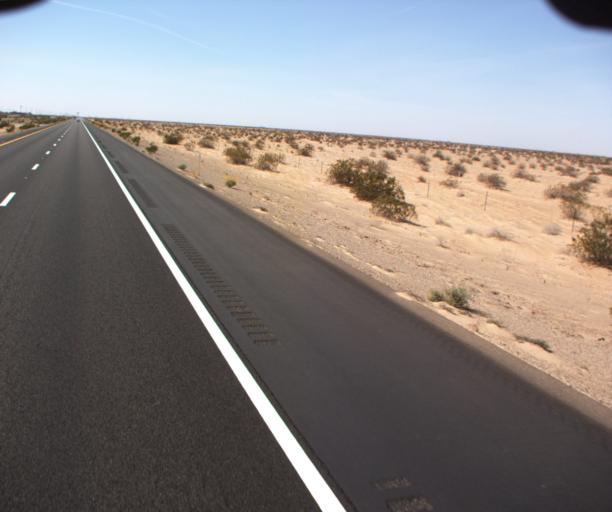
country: US
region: Arizona
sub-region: Yuma County
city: Somerton
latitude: 32.4954
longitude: -114.6230
